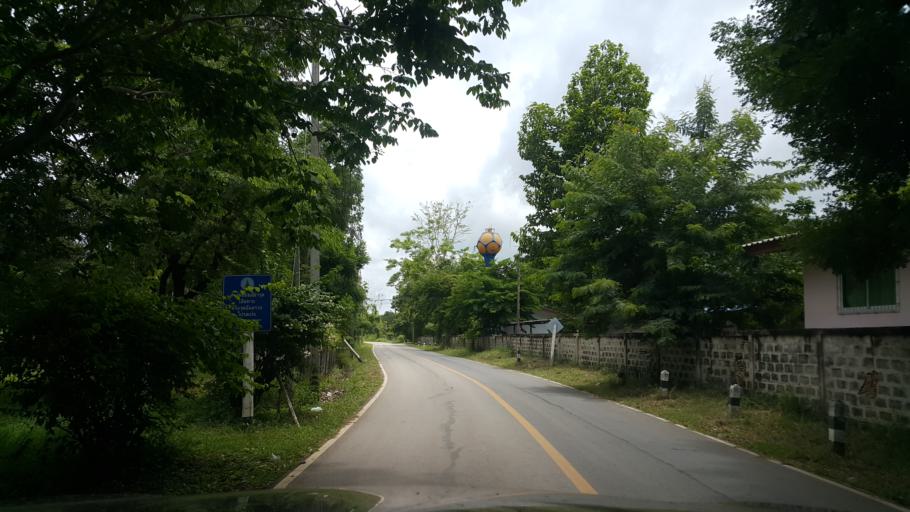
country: TH
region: Sukhothai
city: Kong Krailat
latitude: 16.9339
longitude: 99.9568
